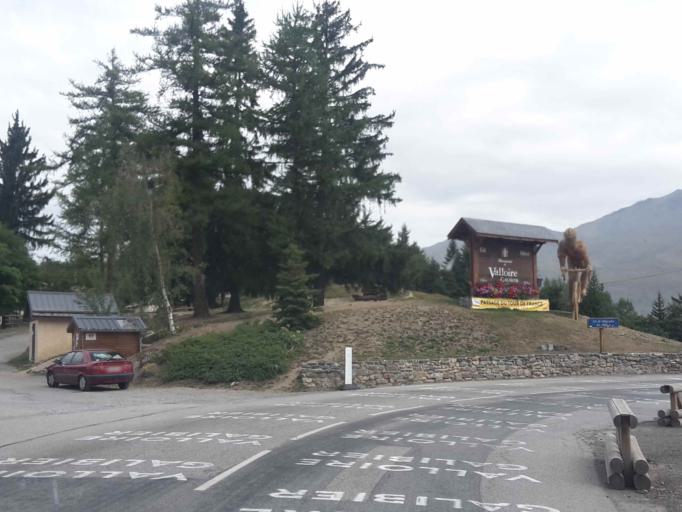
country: FR
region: Rhone-Alpes
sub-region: Departement de la Savoie
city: Saint-Michel-de-Maurienne
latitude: 45.2025
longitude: 6.4443
